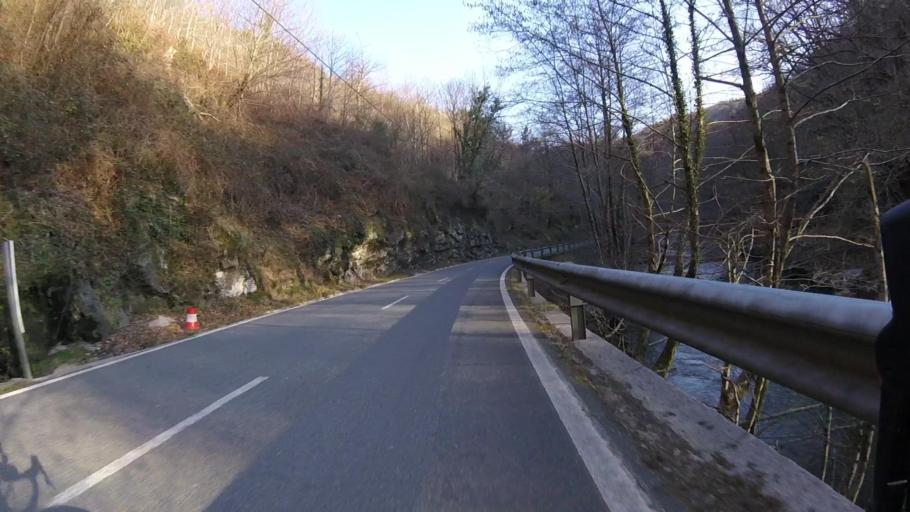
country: ES
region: Navarre
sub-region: Provincia de Navarra
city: Arano
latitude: 43.2105
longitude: -1.8700
